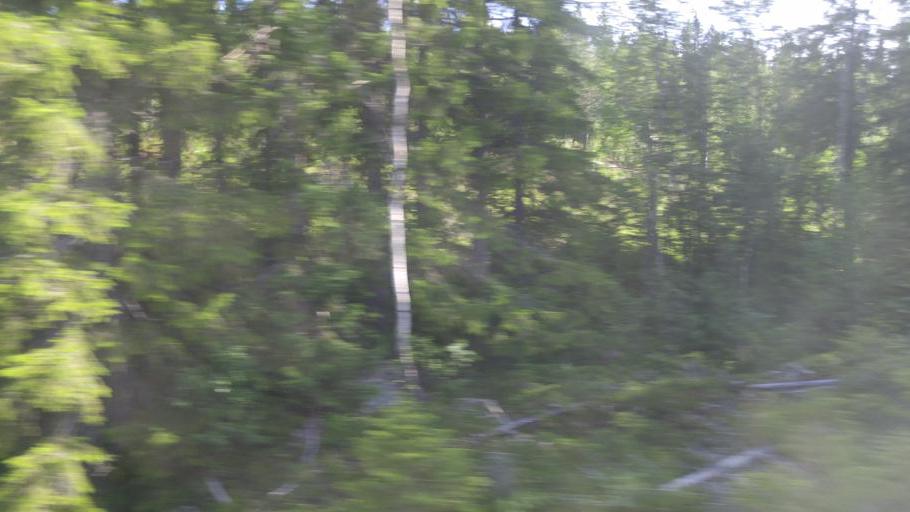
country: NO
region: Nord-Trondelag
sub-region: Meraker
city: Meraker
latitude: 63.4017
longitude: 11.8365
